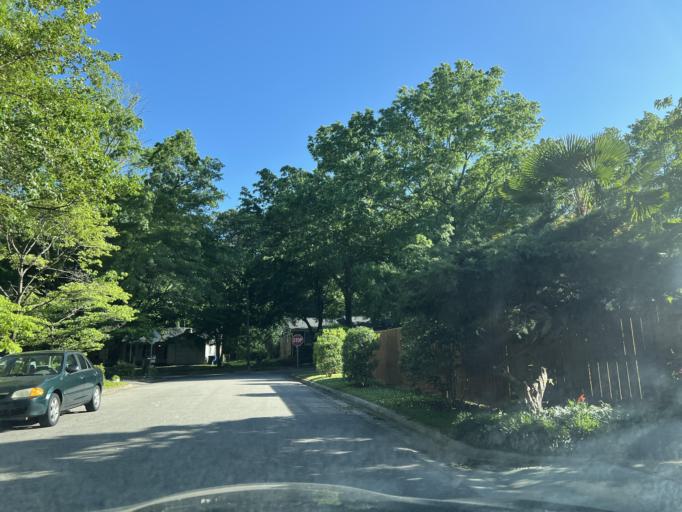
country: US
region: North Carolina
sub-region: Wake County
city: West Raleigh
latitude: 35.8651
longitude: -78.6464
